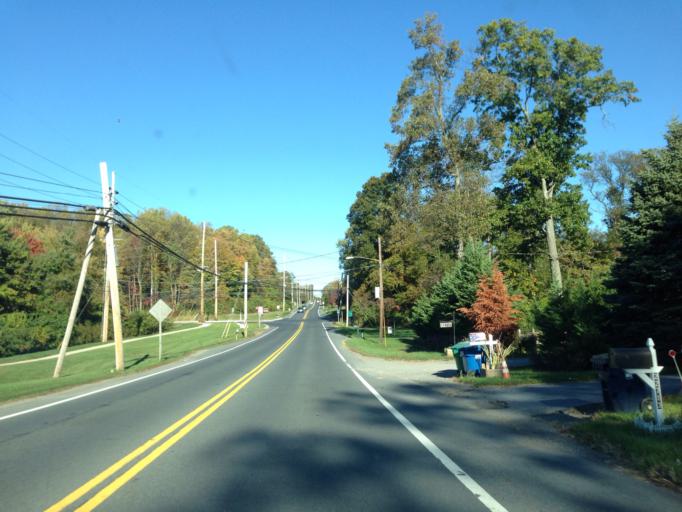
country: US
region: Maryland
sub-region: Montgomery County
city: Clarksburg
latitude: 39.2292
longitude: -77.2673
